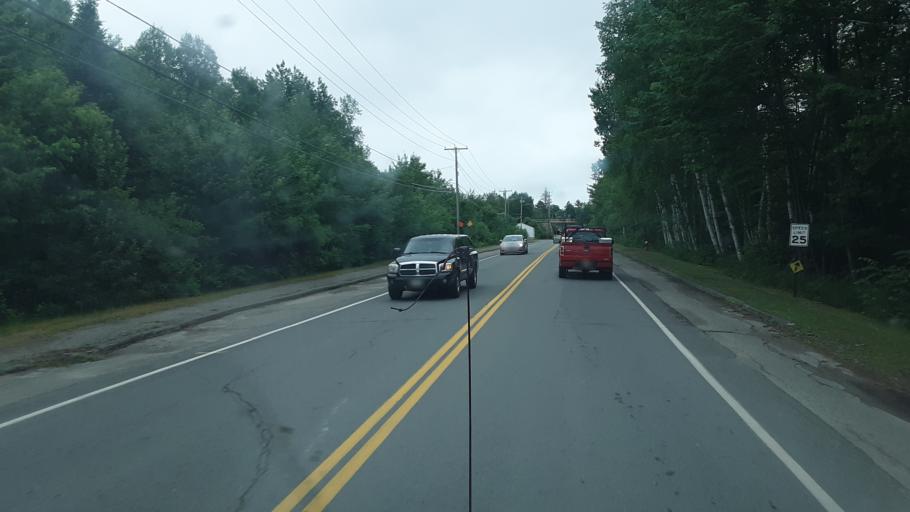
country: US
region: Maine
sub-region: Penobscot County
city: Millinocket
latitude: 45.6660
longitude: -68.7183
